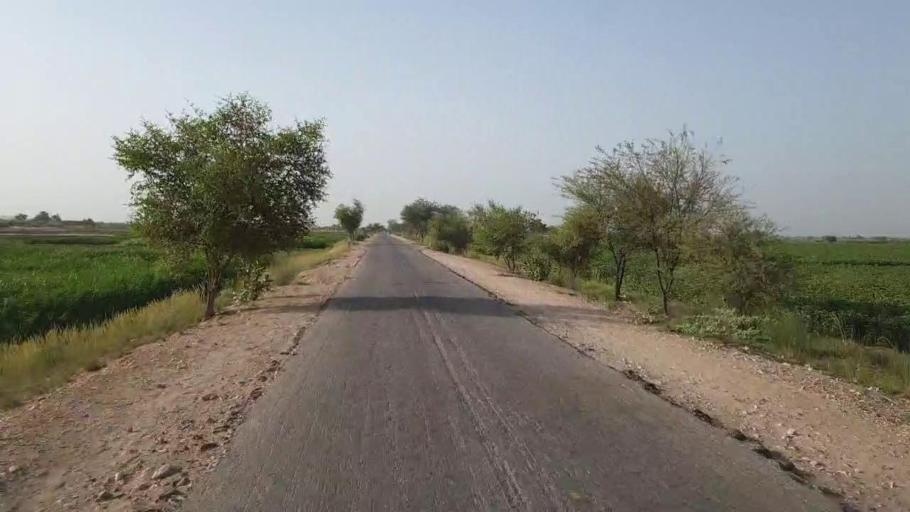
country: PK
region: Sindh
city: Jam Sahib
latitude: 26.4631
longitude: 68.8588
